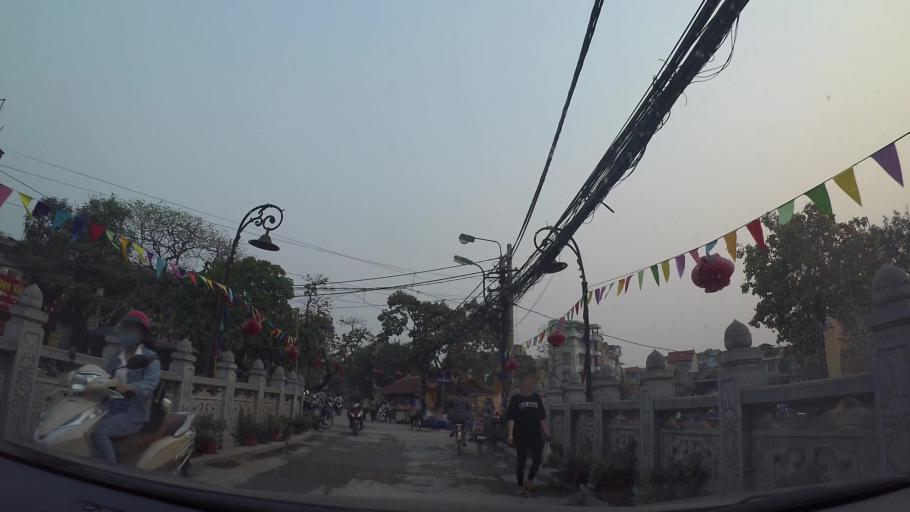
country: VN
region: Ha Noi
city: Thanh Xuan
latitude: 20.9807
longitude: 105.8009
